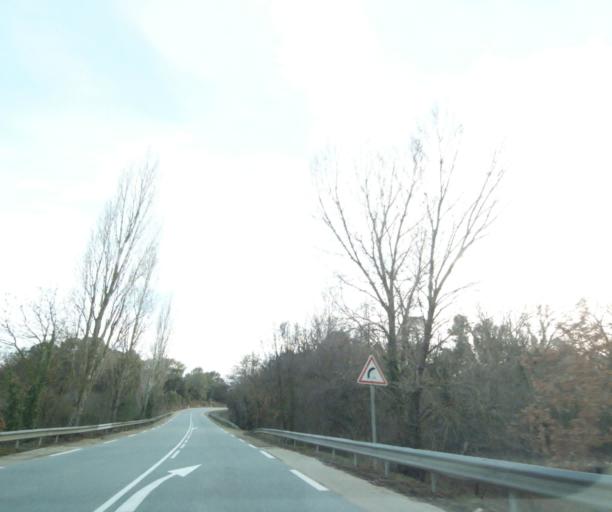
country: FR
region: Provence-Alpes-Cote d'Azur
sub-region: Departement du Var
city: La Motte
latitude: 43.4889
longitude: 6.5117
